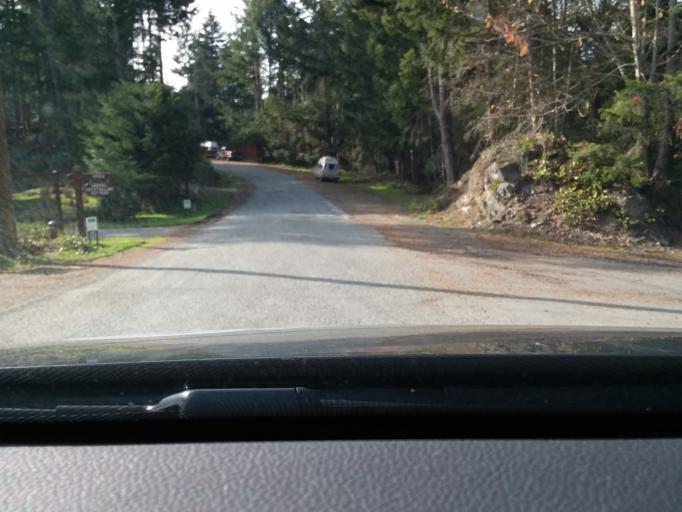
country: CA
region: British Columbia
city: North Saanich
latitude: 48.7692
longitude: -123.2930
